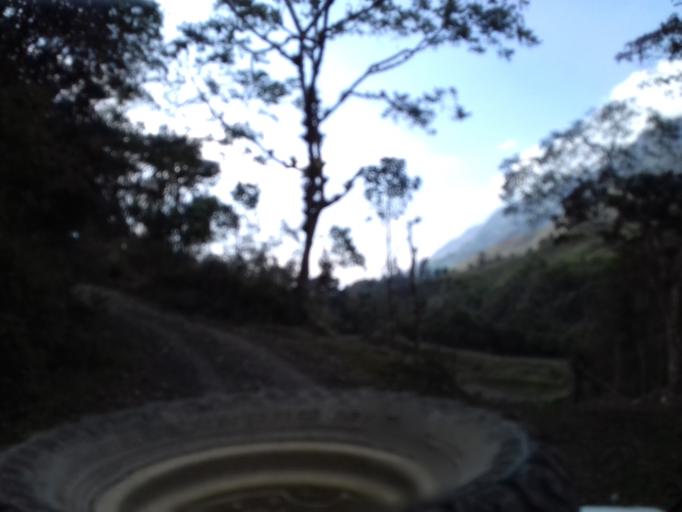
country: CO
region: Tolima
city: Cajamarca
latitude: 4.5319
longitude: -75.4102
